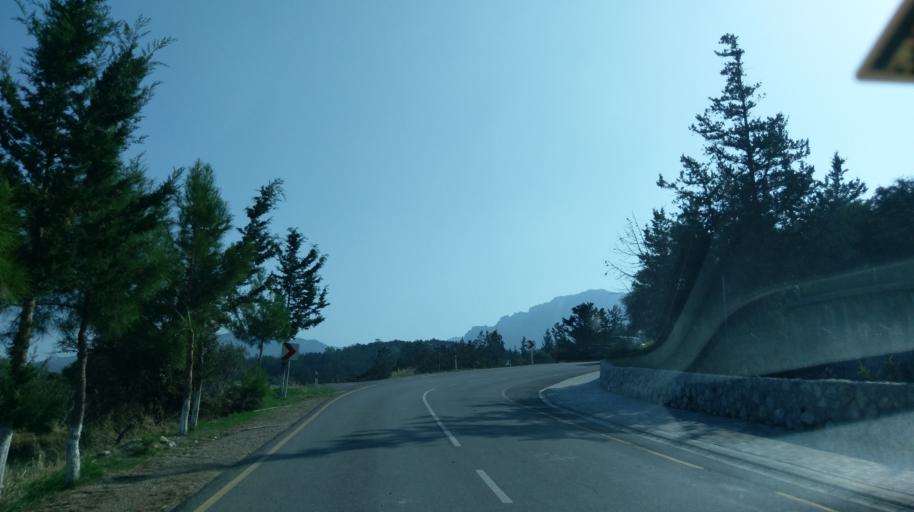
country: CY
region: Ammochostos
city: Lefkonoiko
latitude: 35.3893
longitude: 33.7508
